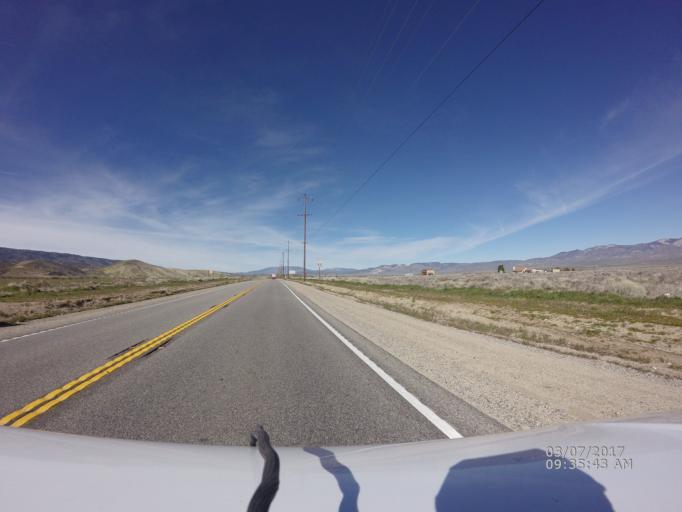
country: US
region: California
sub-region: Los Angeles County
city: Green Valley
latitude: 34.7758
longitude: -118.5905
